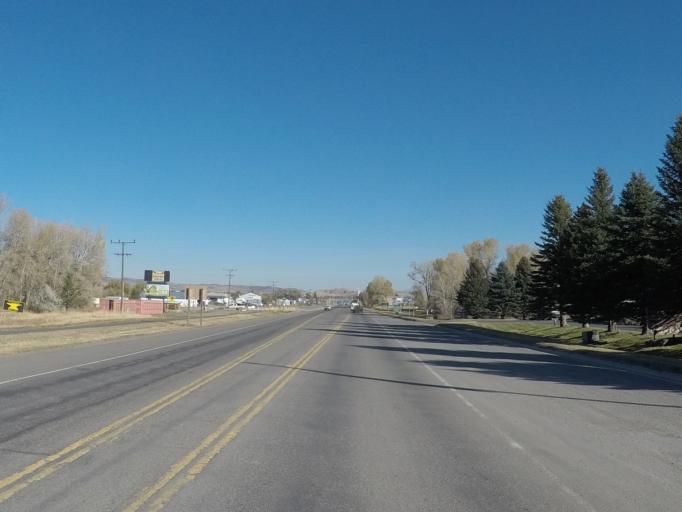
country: US
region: Montana
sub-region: Park County
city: Livingston
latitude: 45.6348
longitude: -110.5757
